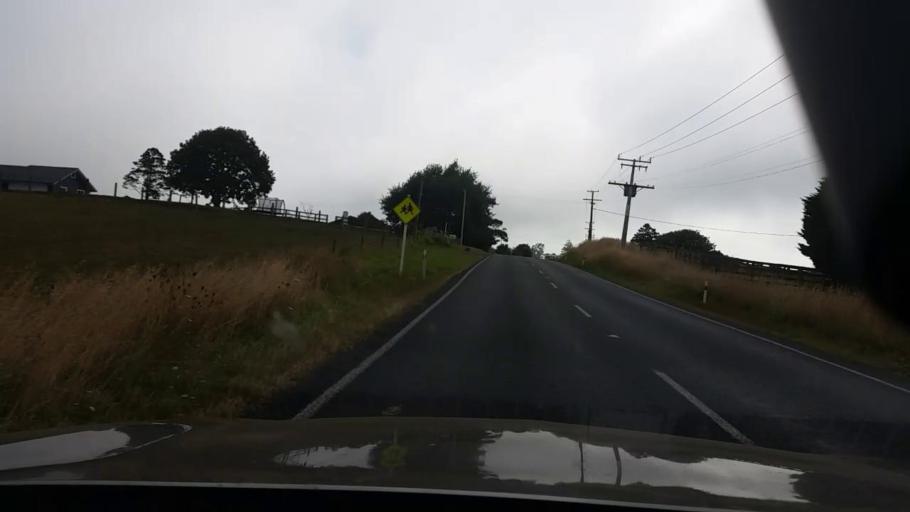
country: NZ
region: Waikato
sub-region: Hamilton City
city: Hamilton
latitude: -37.6215
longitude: 175.3315
